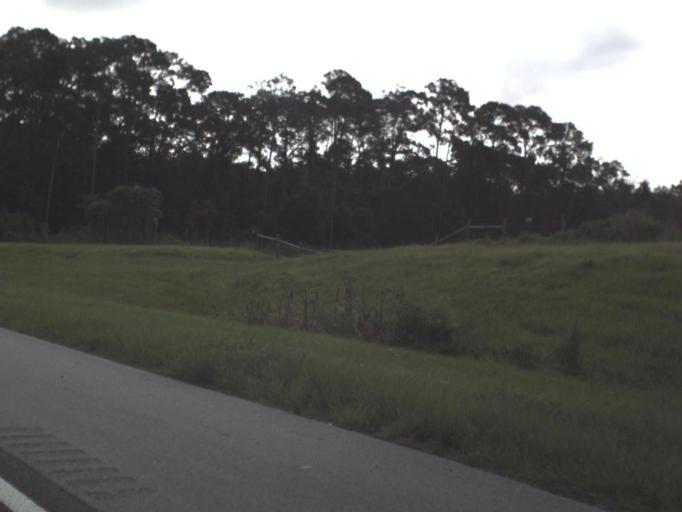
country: US
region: Florida
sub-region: Hillsborough County
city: University
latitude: 28.1076
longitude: -82.4303
